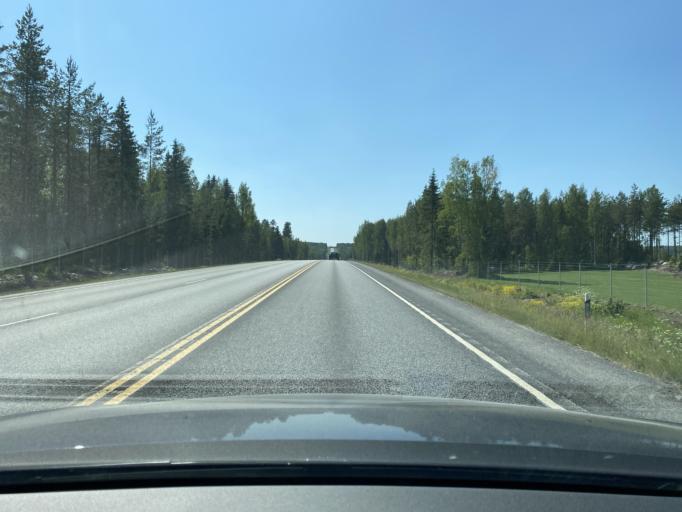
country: FI
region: Pirkanmaa
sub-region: Tampere
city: Nokia
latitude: 61.4028
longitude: 23.2717
